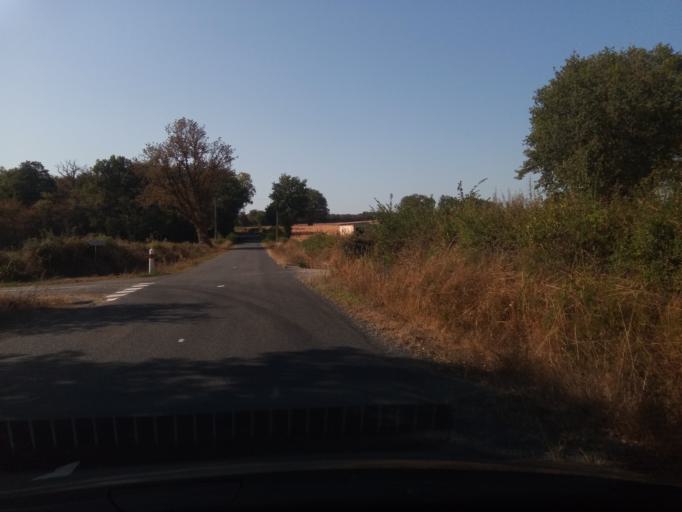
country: FR
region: Poitou-Charentes
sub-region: Departement de la Vienne
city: Saulge
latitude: 46.3541
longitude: 0.8732
